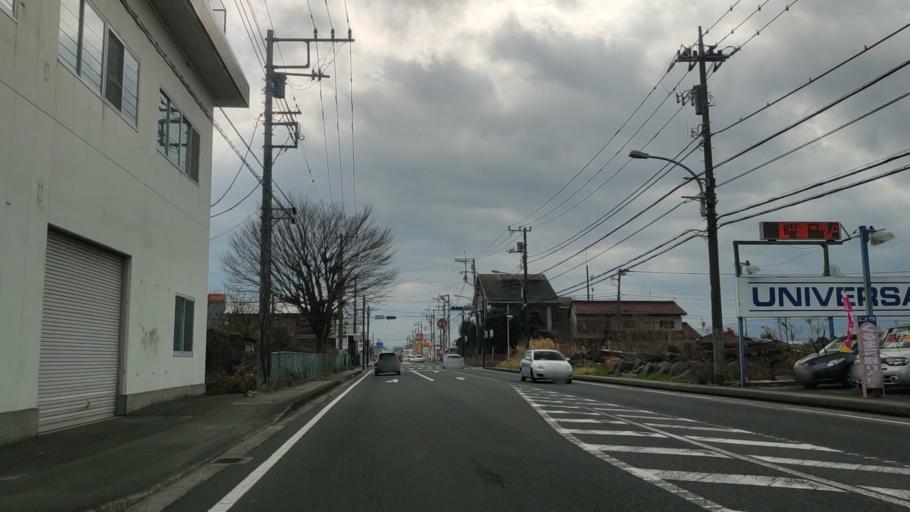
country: JP
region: Kanagawa
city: Odawara
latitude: 35.3017
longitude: 139.1667
